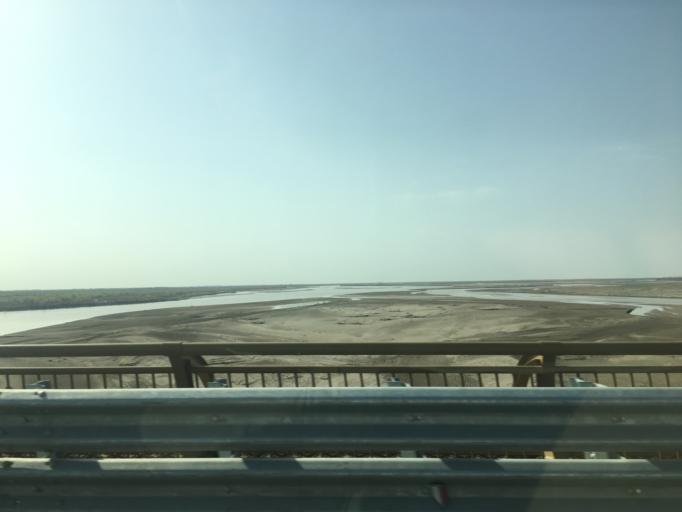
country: TM
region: Lebap
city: Farap
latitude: 39.1319
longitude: 63.5692
